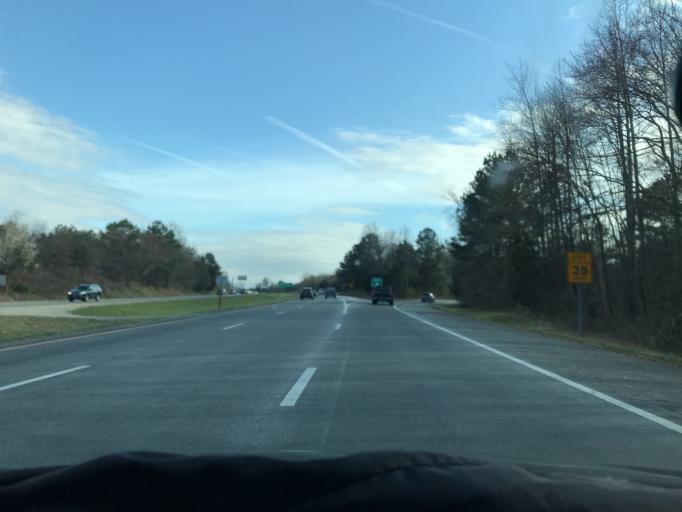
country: US
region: Virginia
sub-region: Chesterfield County
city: Brandermill
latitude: 37.4273
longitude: -77.6325
